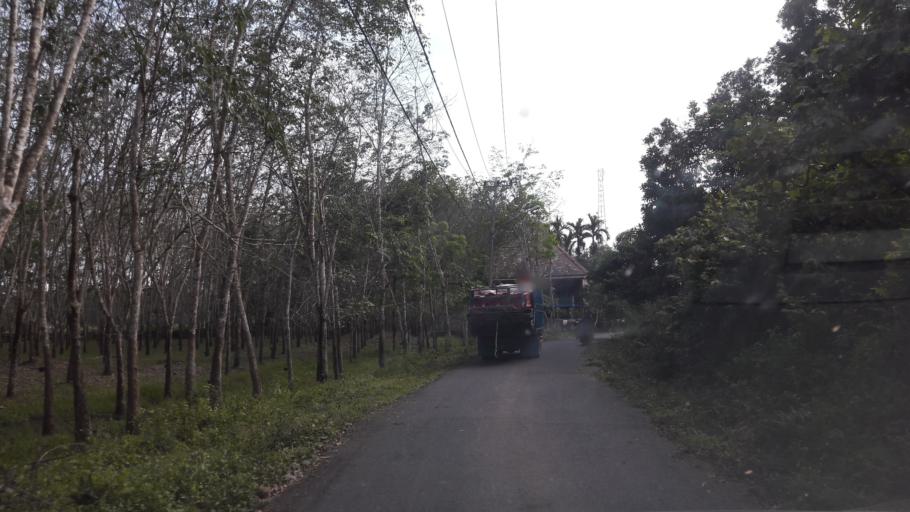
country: ID
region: South Sumatra
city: Gunungmenang
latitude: -3.1099
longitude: 103.9516
